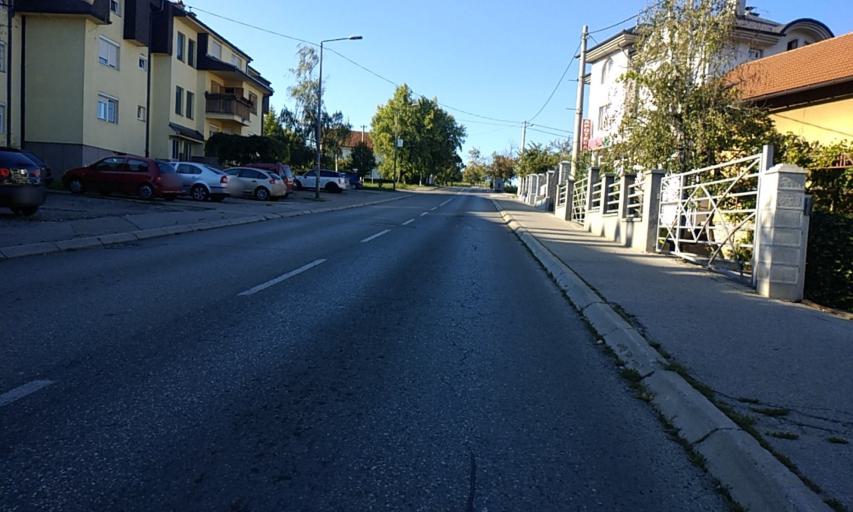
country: BA
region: Republika Srpska
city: Banja Luka
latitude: 44.7804
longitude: 17.1778
